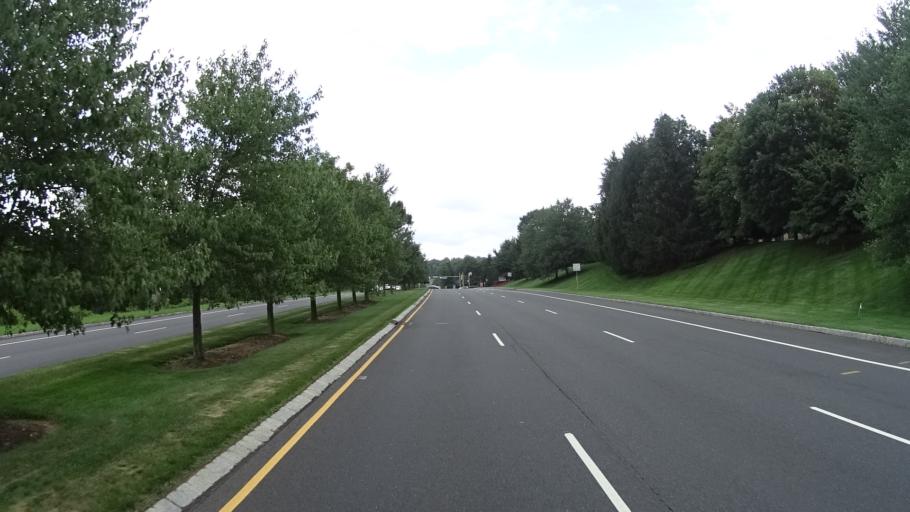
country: US
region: New Jersey
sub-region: Somerset County
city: Warren Township
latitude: 40.6460
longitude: -74.5206
